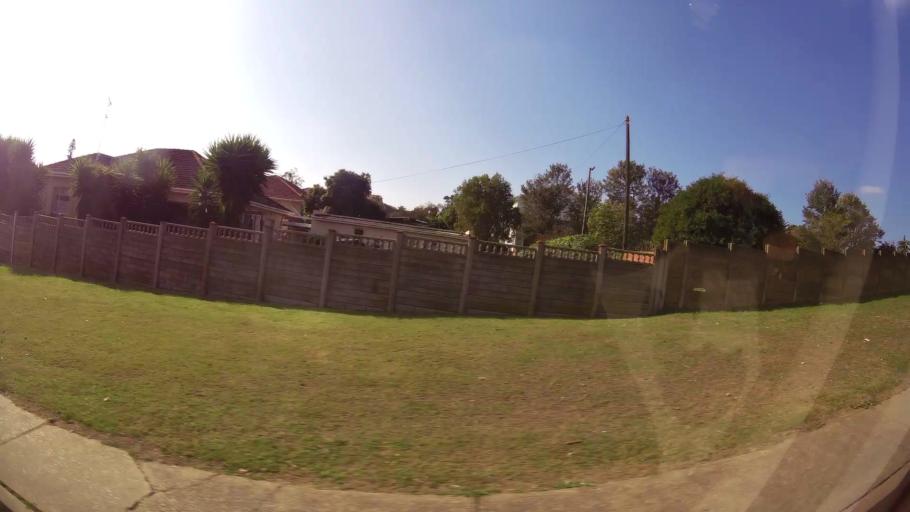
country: ZA
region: Eastern Cape
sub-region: Nelson Mandela Bay Metropolitan Municipality
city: Uitenhage
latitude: -33.7705
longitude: 25.4161
